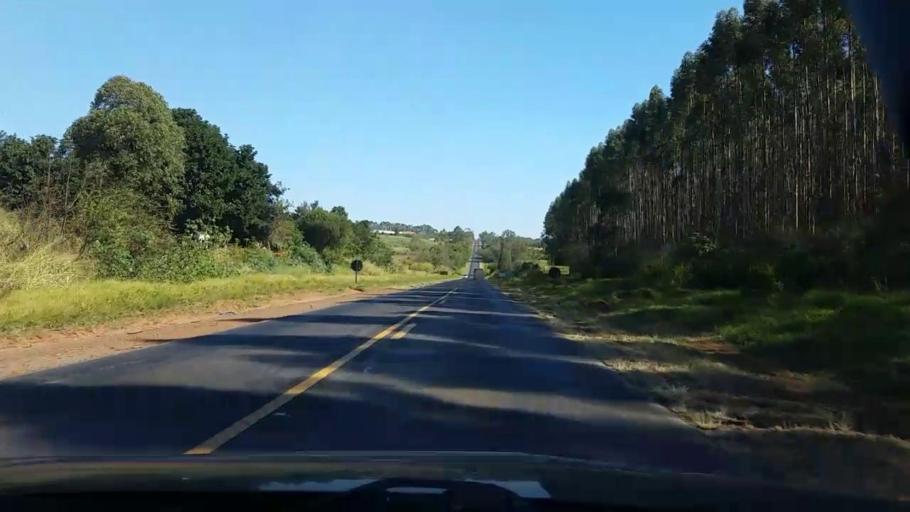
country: BR
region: Sao Paulo
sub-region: Sao Manuel
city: Sao Manuel
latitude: -22.8074
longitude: -48.6727
